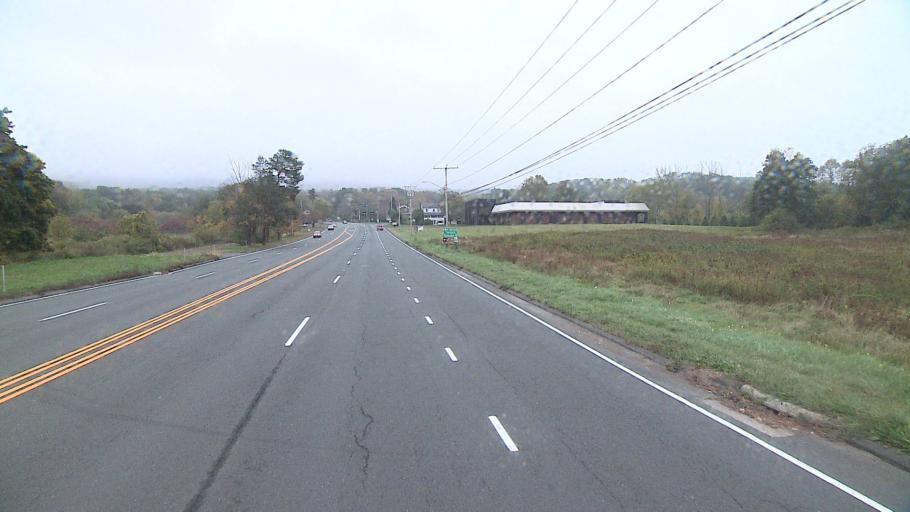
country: US
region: Connecticut
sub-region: Hartford County
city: Weatogue
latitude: 41.8059
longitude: -72.8201
